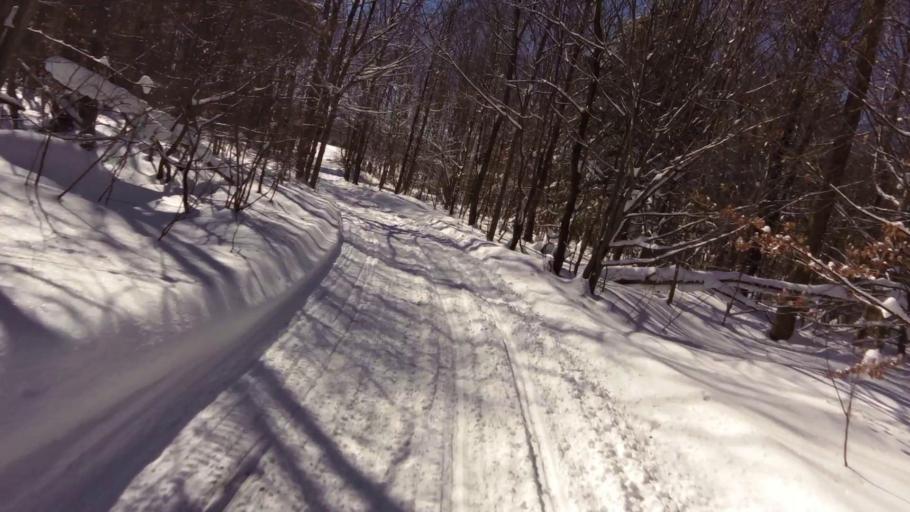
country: US
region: New York
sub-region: Chautauqua County
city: Mayville
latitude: 42.1992
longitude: -79.5404
